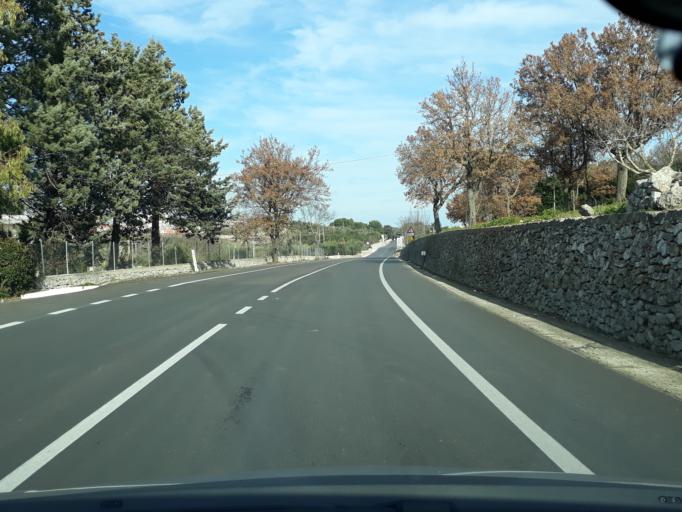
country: IT
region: Apulia
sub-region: Provincia di Bari
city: Locorotondo
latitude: 40.7849
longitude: 17.3404
